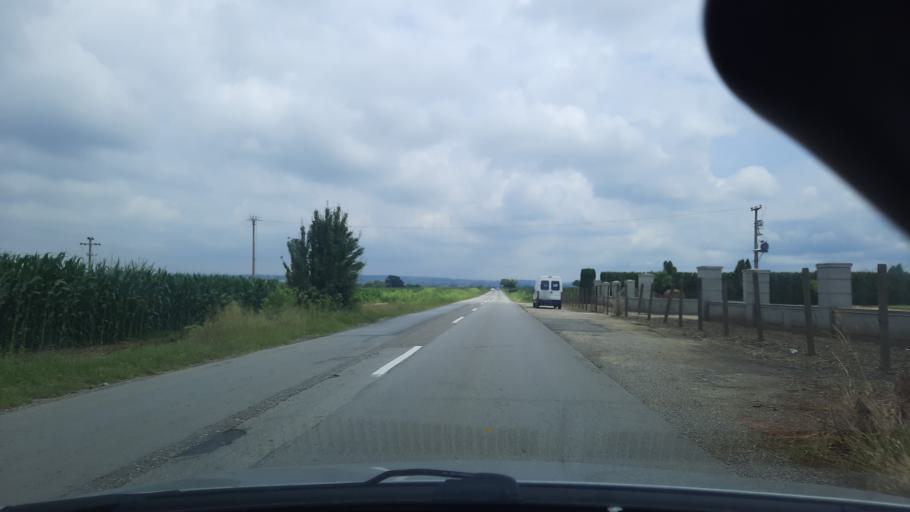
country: RS
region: Central Serbia
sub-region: Branicevski Okrug
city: Malo Crnice
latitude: 44.5835
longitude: 21.3008
